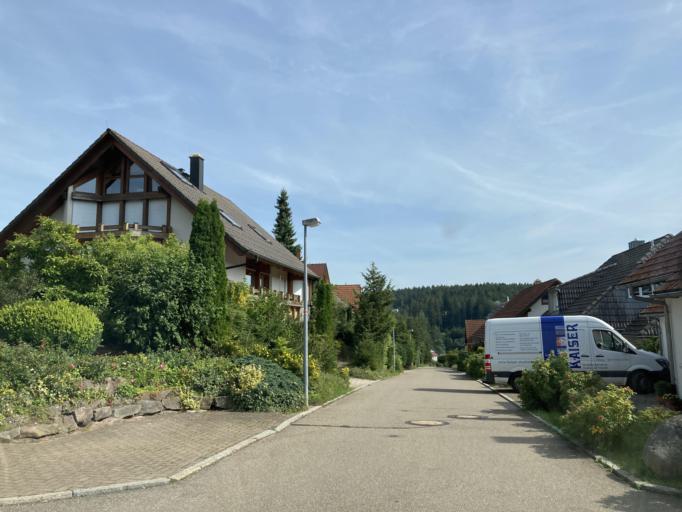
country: DE
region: Baden-Wuerttemberg
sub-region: Freiburg Region
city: Sankt Georgen im Schwarzwald
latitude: 48.1176
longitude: 8.3060
